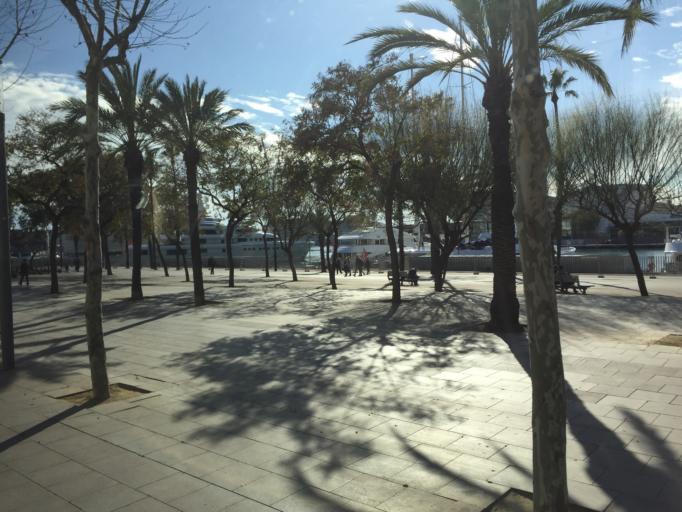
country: ES
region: Catalonia
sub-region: Provincia de Barcelona
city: Ciutat Vella
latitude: 41.3792
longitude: 2.1876
